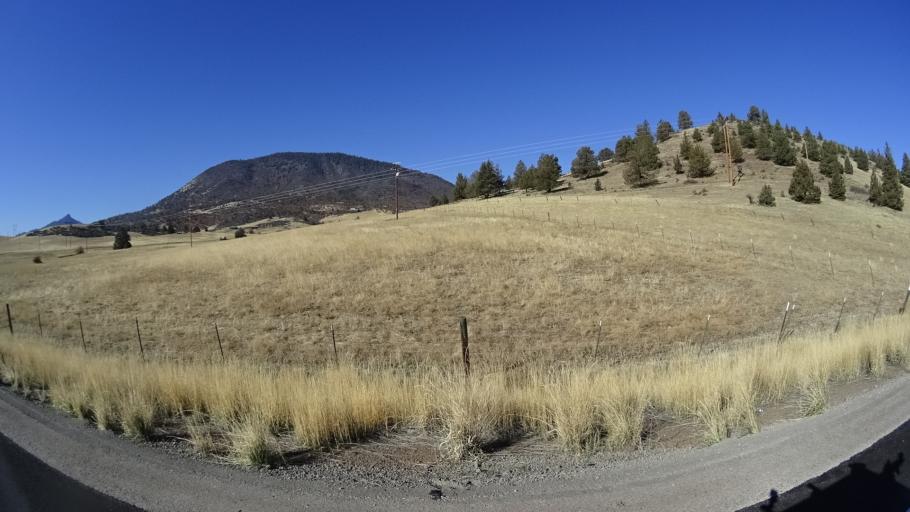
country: US
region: California
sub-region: Siskiyou County
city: Montague
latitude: 41.8593
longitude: -122.4643
